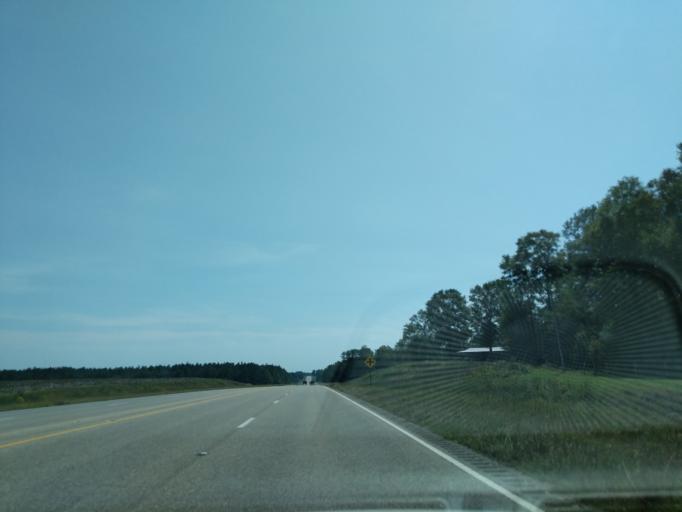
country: US
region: Alabama
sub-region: Covington County
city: Andalusia
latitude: 31.3864
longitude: -86.5703
